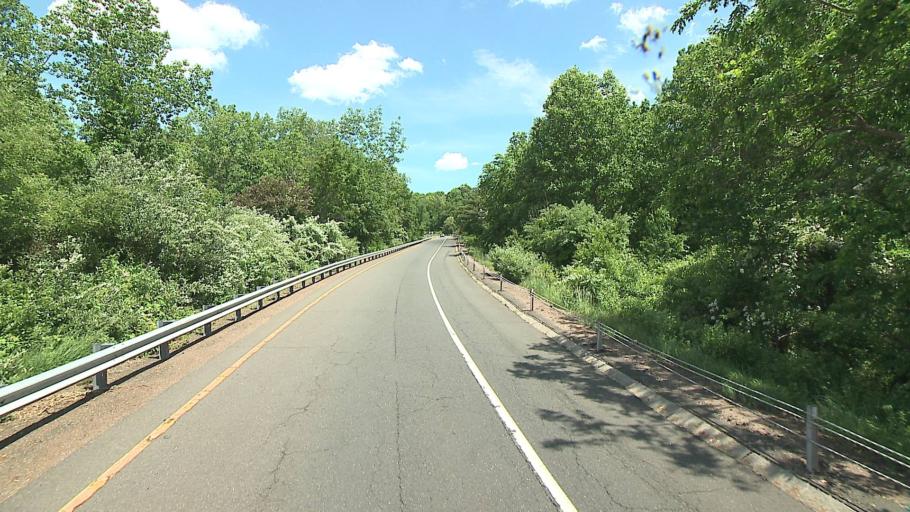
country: US
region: Connecticut
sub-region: New Haven County
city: Meriden
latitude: 41.5539
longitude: -72.8509
